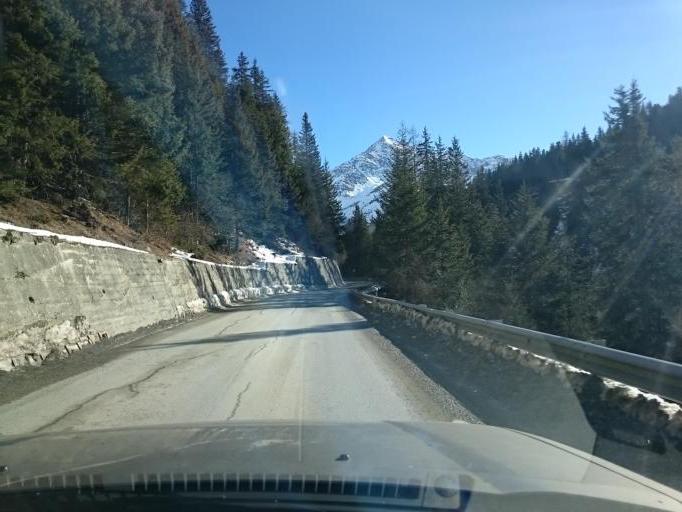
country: IT
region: Lombardy
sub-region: Provincia di Sondrio
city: Sant'Antonio
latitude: 46.4194
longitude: 10.4772
